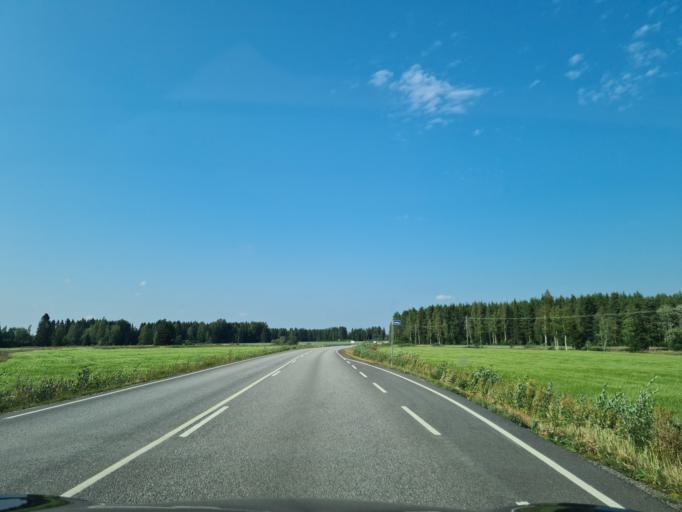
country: FI
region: Satakunta
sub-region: Pohjois-Satakunta
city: Kankaanpaeae
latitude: 61.9071
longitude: 22.4993
